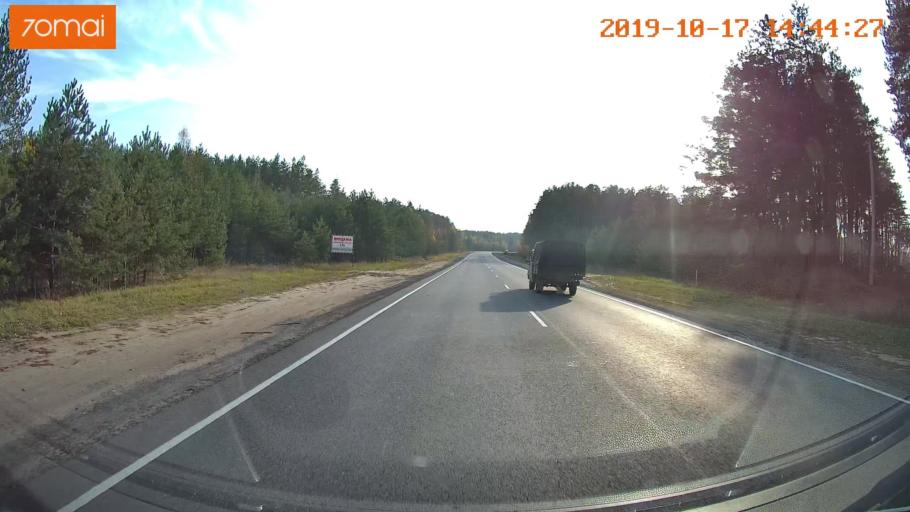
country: RU
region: Rjazan
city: Solotcha
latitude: 54.8128
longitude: 39.8916
